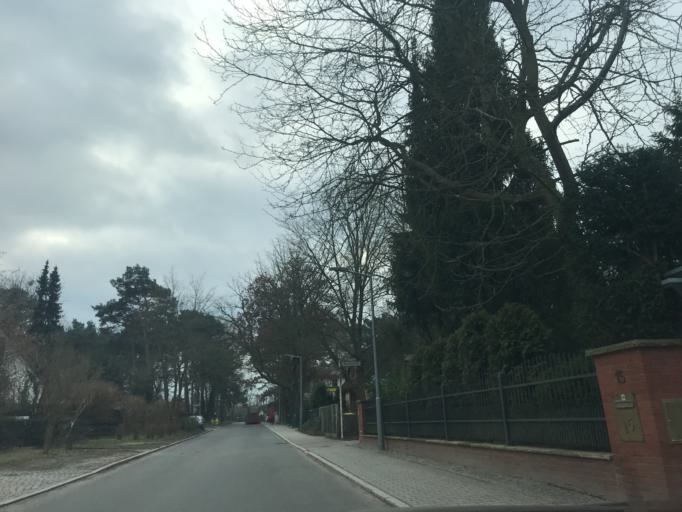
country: DE
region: Berlin
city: Kladow
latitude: 52.4523
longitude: 13.1220
